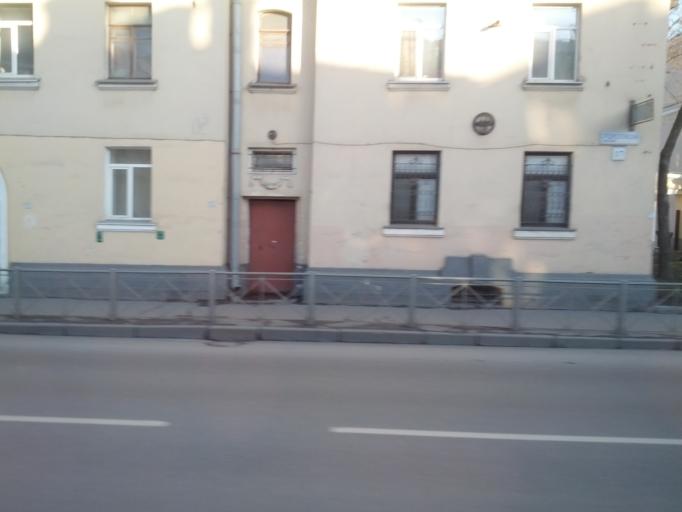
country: RU
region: Leningrad
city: Kalininskiy
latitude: 59.9517
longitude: 30.4149
